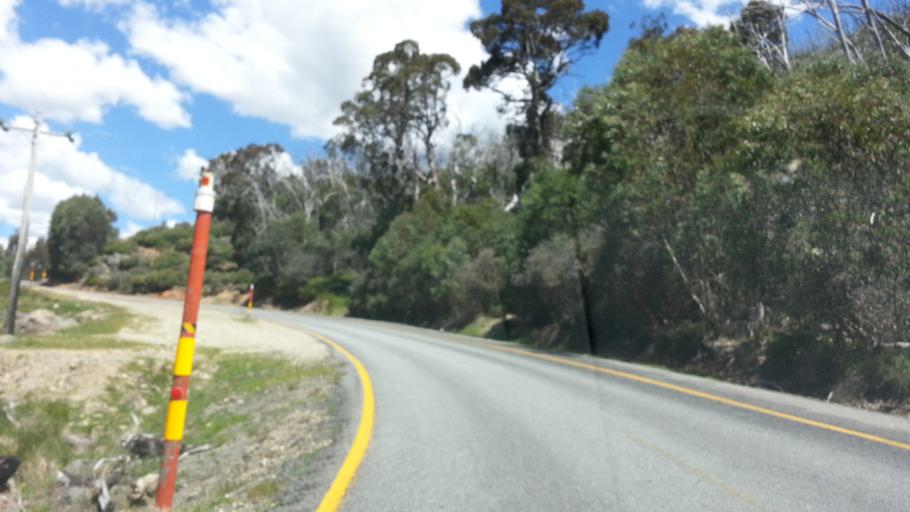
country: AU
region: Victoria
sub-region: Alpine
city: Mount Beauty
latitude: -36.8495
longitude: 147.2691
